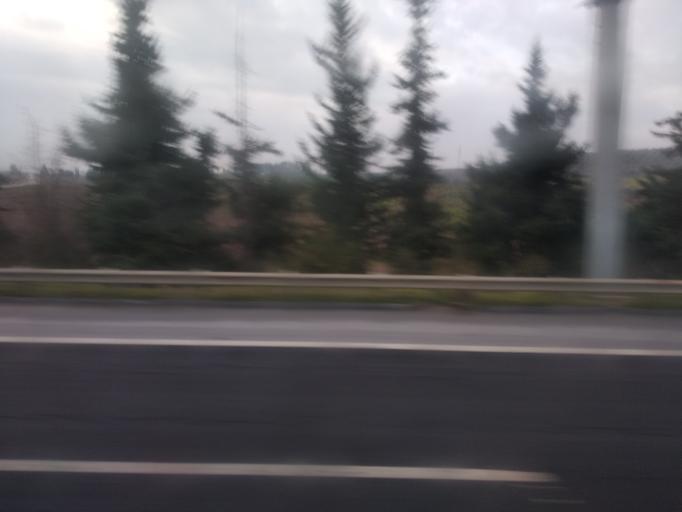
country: TR
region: Mersin
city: Yenice
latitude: 37.0395
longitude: 35.1647
